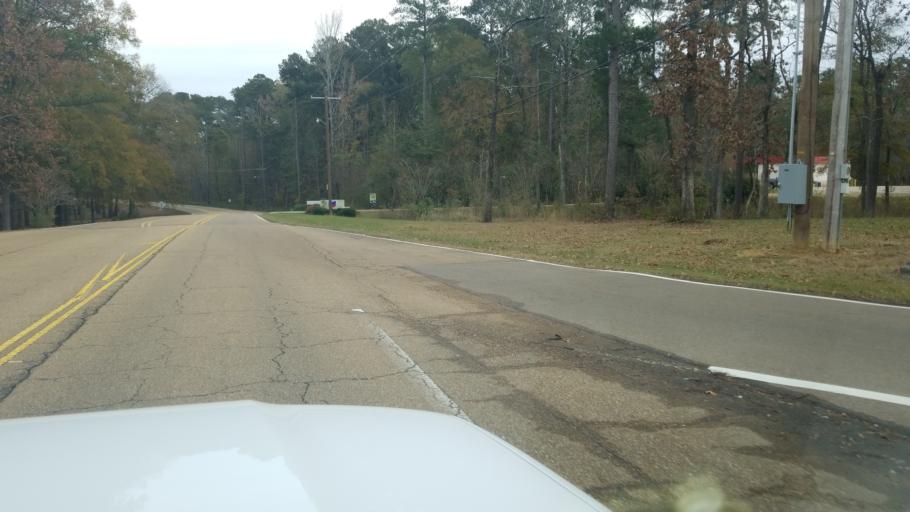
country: US
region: Mississippi
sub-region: Rankin County
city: Brandon
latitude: 32.3725
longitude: -90.0169
